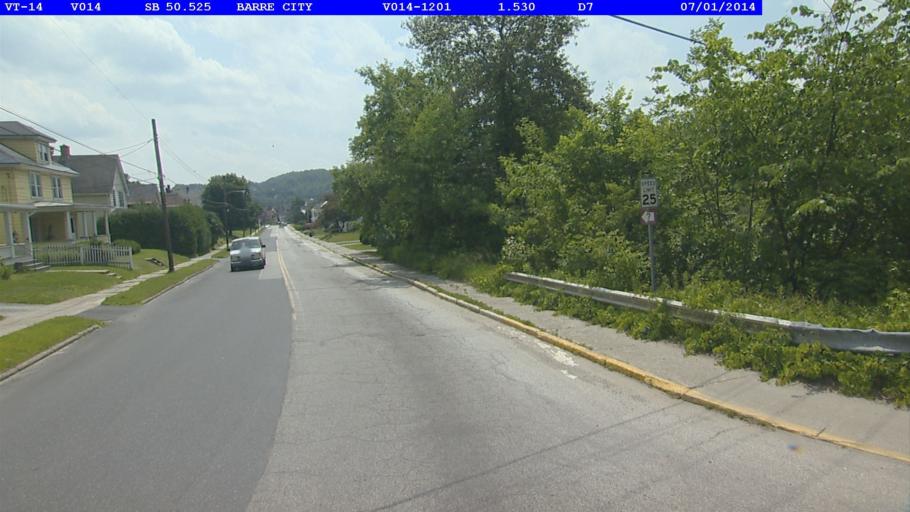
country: US
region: Vermont
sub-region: Washington County
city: Barre
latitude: 44.2069
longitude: -72.5043
